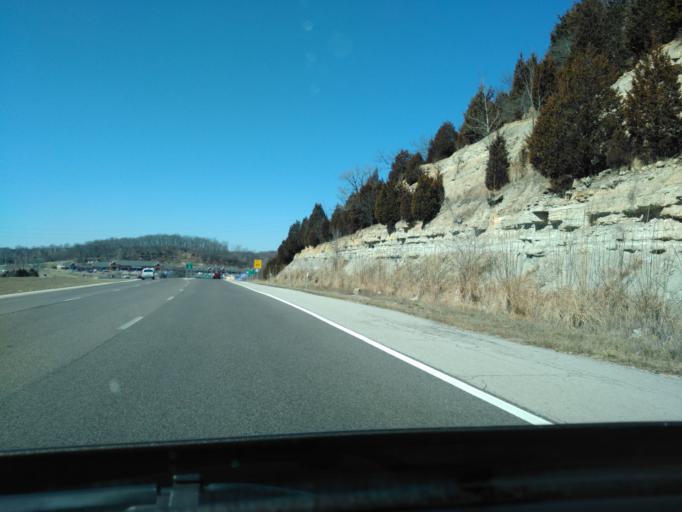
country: US
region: Missouri
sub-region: Saint Louis County
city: Fenton
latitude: 38.5157
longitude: -90.4419
